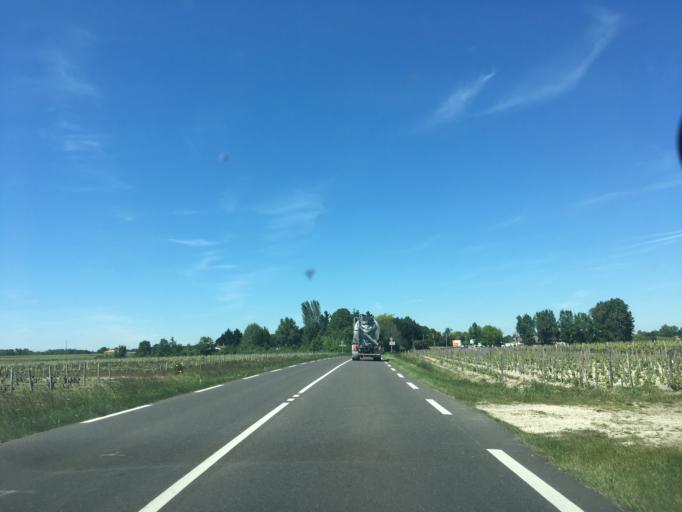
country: FR
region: Aquitaine
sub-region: Departement de la Gironde
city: Listrac-Medoc
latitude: 45.0646
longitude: -0.7952
